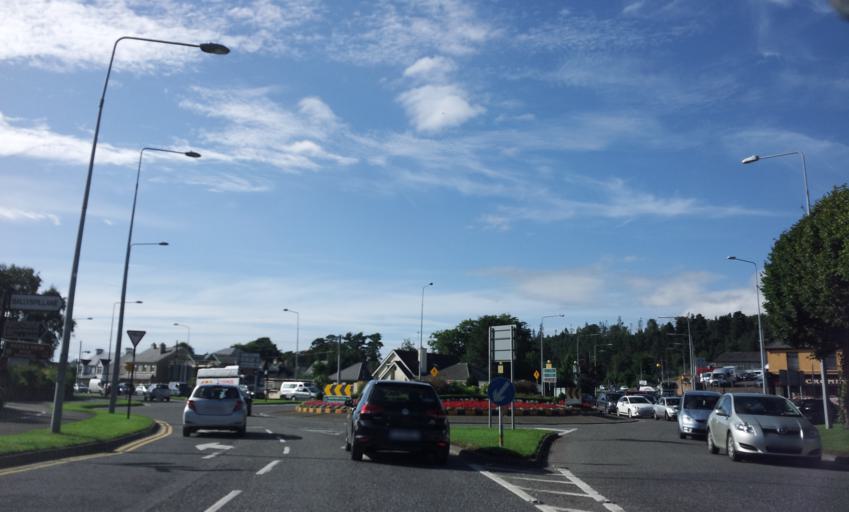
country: IE
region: Munster
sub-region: Ciarrai
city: Cill Airne
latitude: 52.0601
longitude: -9.4825
